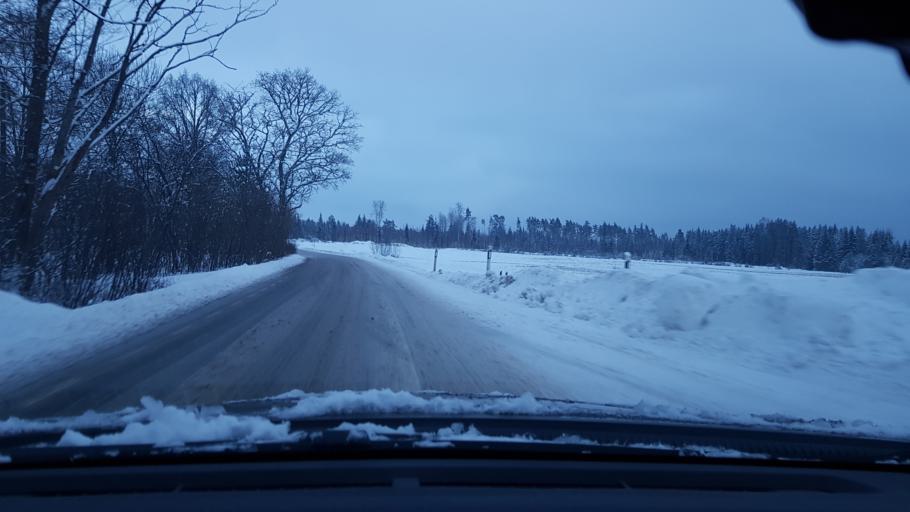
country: EE
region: Raplamaa
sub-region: Rapla vald
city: Rapla
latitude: 58.9230
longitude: 24.6554
